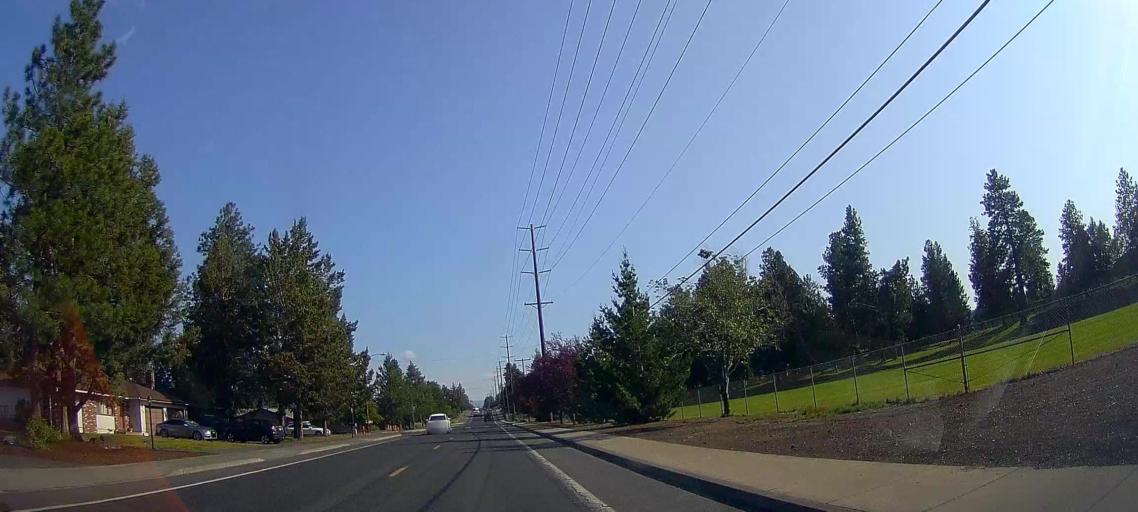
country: US
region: Oregon
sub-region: Deschutes County
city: Bend
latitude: 44.0480
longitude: -121.2839
